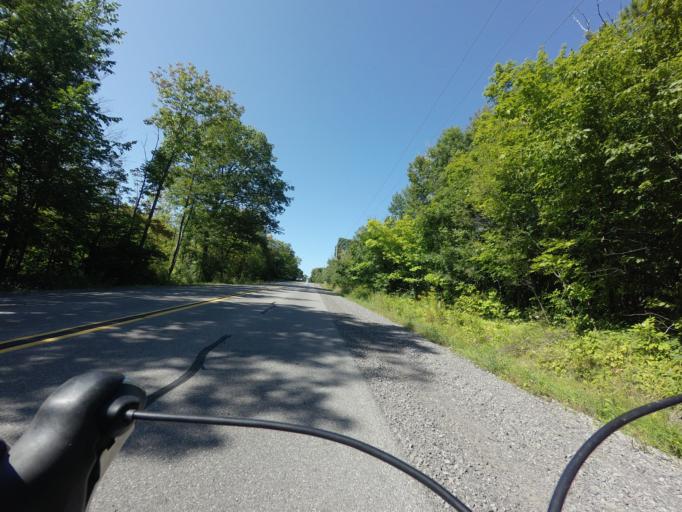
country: CA
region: Ontario
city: Bells Corners
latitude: 45.4068
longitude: -75.9287
